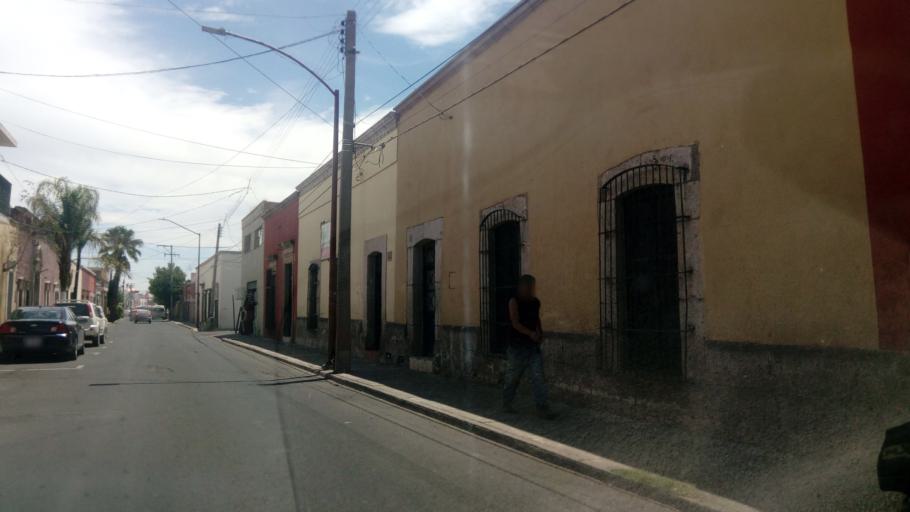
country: MX
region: Durango
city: Victoria de Durango
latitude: 24.0264
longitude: -104.6666
